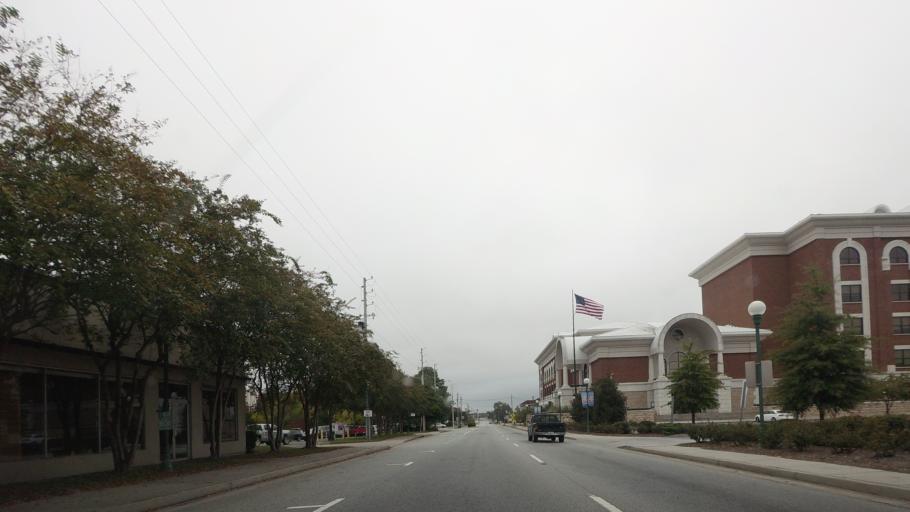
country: US
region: Georgia
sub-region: Lowndes County
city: Valdosta
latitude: 30.8336
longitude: -83.2792
